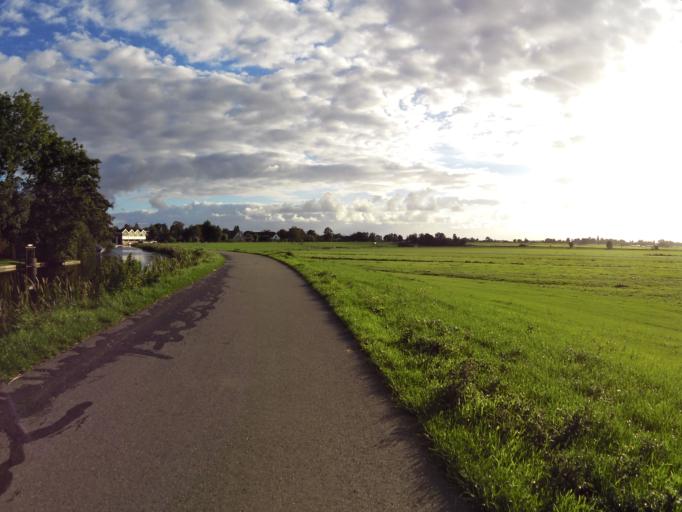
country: NL
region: South Holland
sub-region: Gemeente Nieuwkoop
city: Nieuwkoop
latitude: 52.1367
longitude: 4.7655
